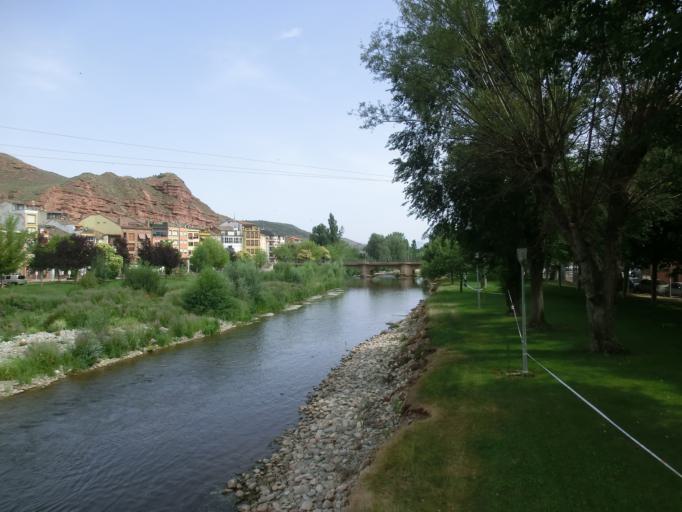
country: ES
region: La Rioja
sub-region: Provincia de La Rioja
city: Najera
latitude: 42.4158
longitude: -2.7328
